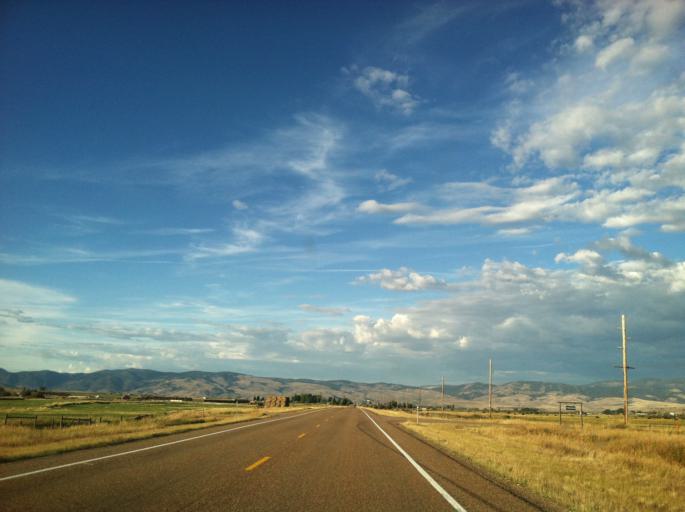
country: US
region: Montana
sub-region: Granite County
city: Philipsburg
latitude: 46.5708
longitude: -113.2064
